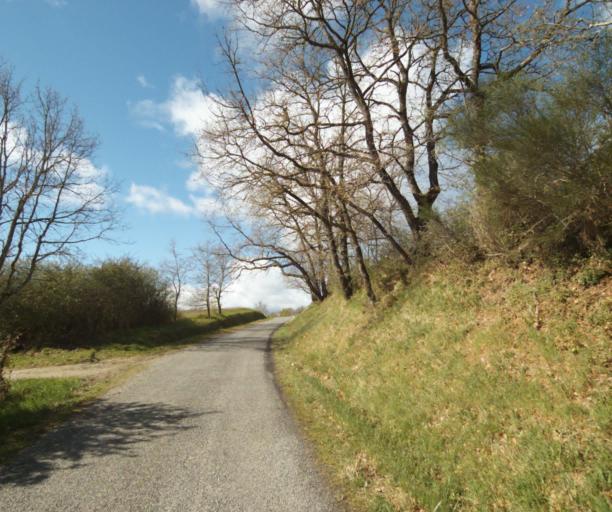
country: FR
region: Midi-Pyrenees
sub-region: Departement de la Haute-Garonne
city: Gaillac-Toulza
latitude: 43.2235
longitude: 1.5137
